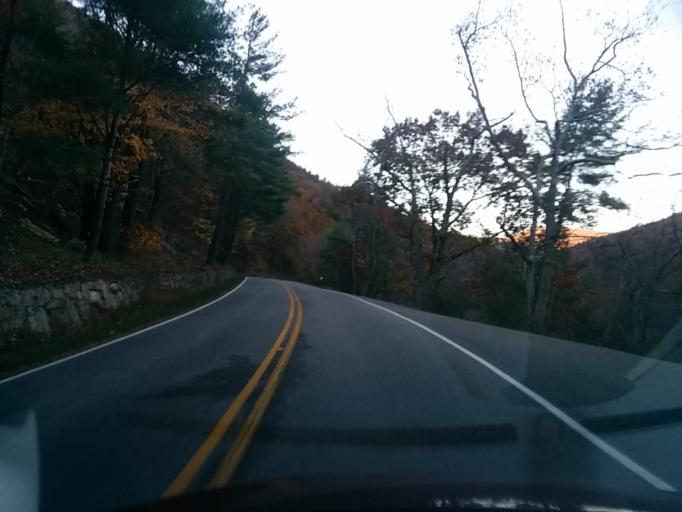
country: US
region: Virginia
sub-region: Rockbridge County
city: East Lexington
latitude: 37.9310
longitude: -79.4490
